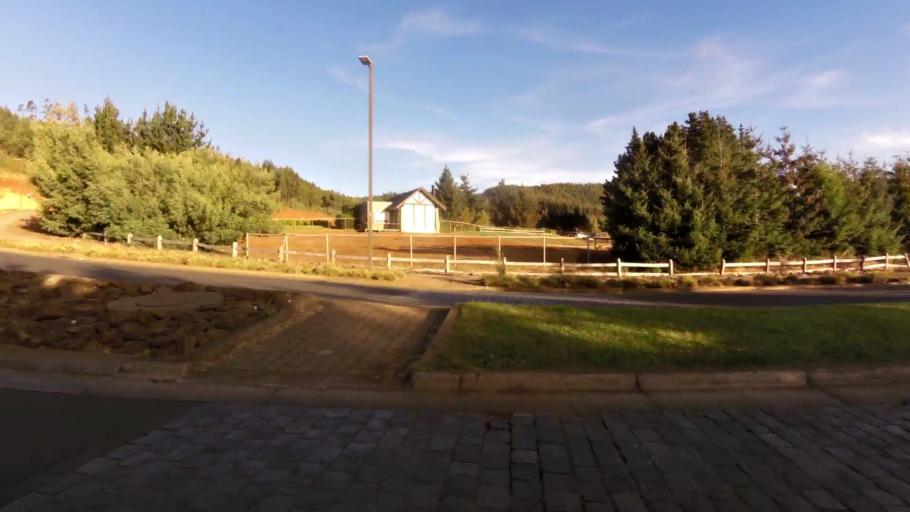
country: CL
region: Biobio
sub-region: Provincia de Concepcion
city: Concepcion
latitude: -36.8633
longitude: -73.0969
